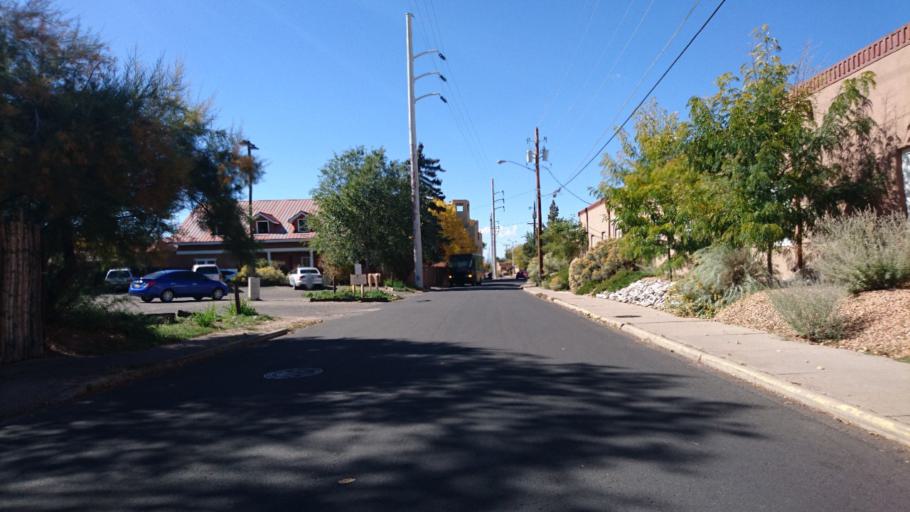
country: US
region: New Mexico
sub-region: Santa Fe County
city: Santa Fe
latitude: 35.6823
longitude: -105.9431
